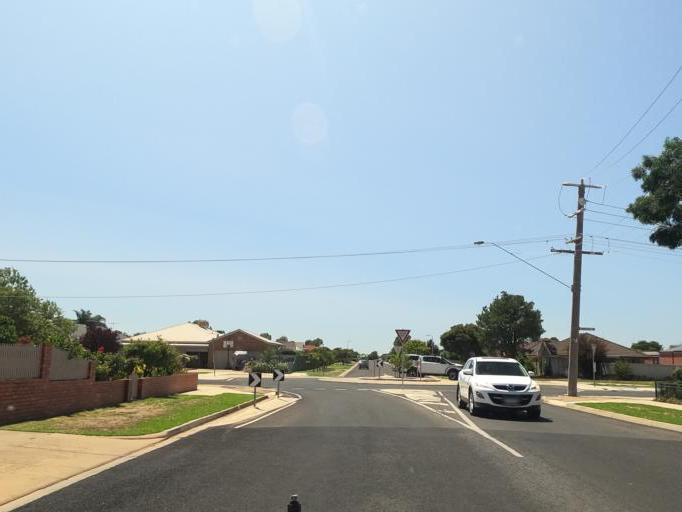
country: AU
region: Victoria
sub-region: Moira
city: Yarrawonga
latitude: -36.0091
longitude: 146.0127
